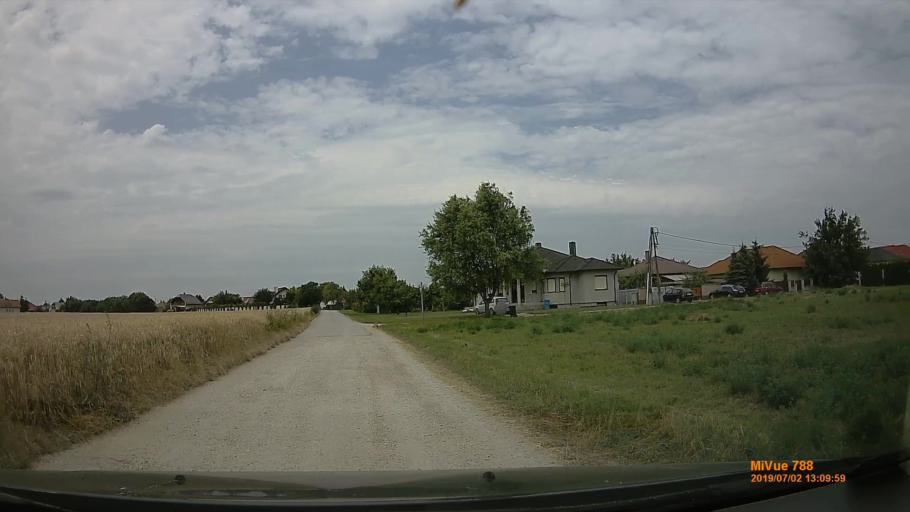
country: HU
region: Gyor-Moson-Sopron
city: Halaszi
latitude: 47.8547
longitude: 17.3254
